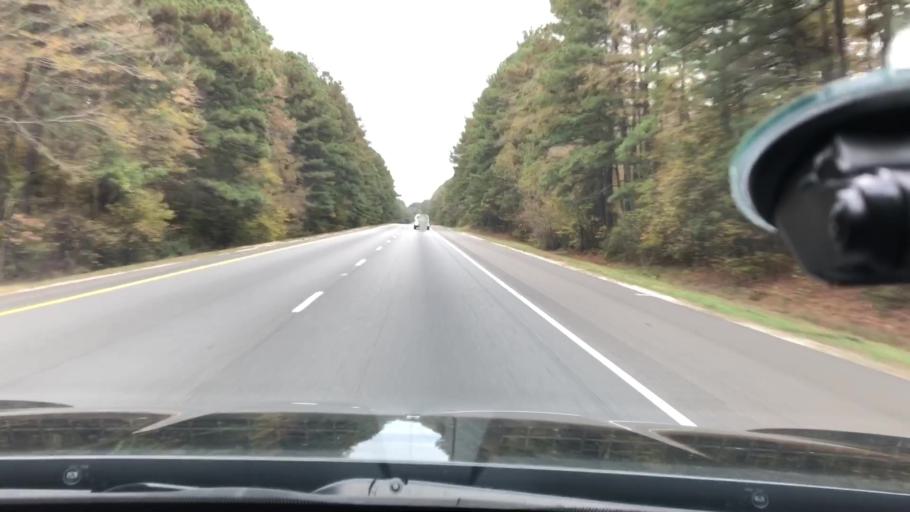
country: US
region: Arkansas
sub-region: Hot Spring County
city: Malvern
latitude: 34.3011
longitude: -92.9450
